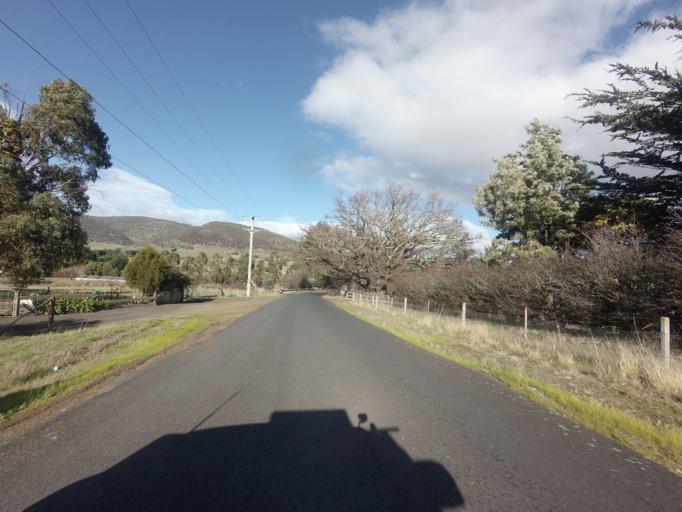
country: AU
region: Tasmania
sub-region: Derwent Valley
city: New Norfolk
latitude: -42.7483
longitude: 147.0456
